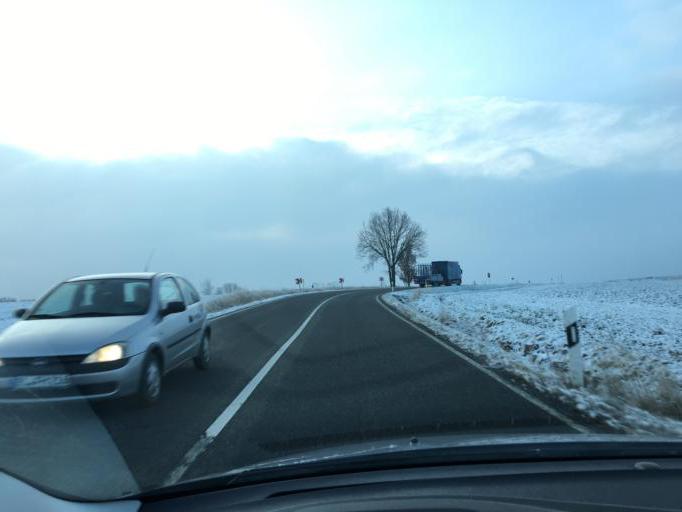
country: DE
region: Saxony
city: Narsdorf
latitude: 50.9832
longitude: 12.6999
